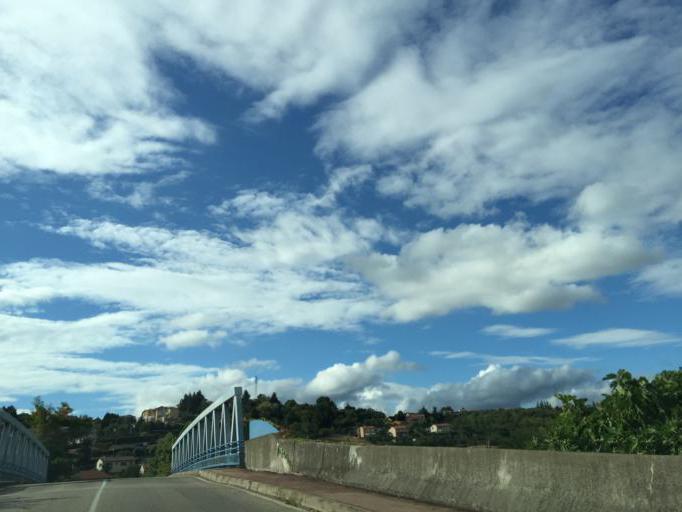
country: FR
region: Rhone-Alpes
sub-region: Departement de la Loire
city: La Grand-Croix
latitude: 45.4962
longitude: 4.5576
